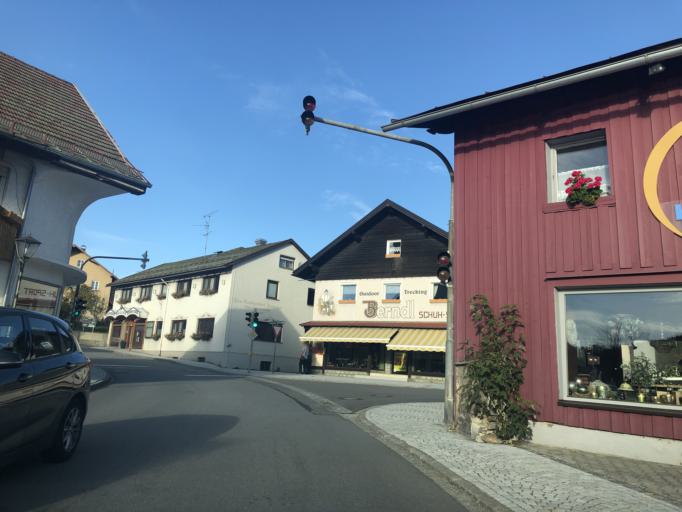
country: DE
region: Bavaria
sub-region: Lower Bavaria
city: Frauenau
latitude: 48.9890
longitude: 13.3007
